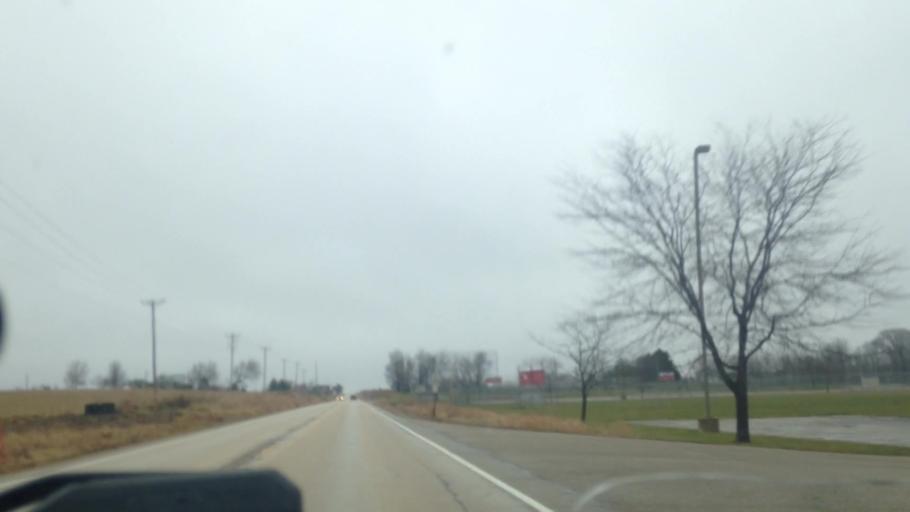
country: US
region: Wisconsin
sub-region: Dodge County
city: Mayville
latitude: 43.4969
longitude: -88.5711
